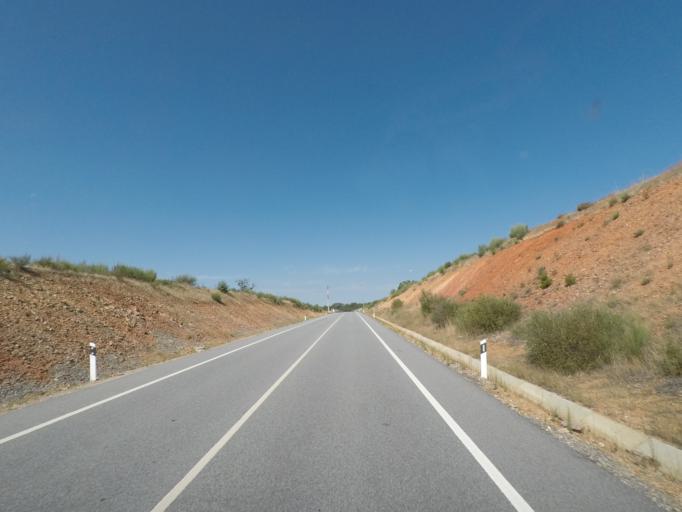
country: PT
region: Braganca
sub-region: Mogadouro
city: Mogadouro
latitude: 41.3454
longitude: -6.6318
